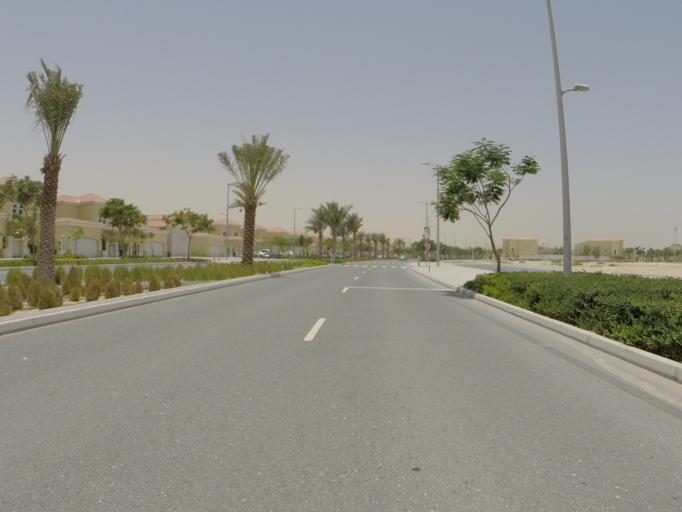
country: AE
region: Dubai
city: Dubai
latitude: 25.0388
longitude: 55.1668
